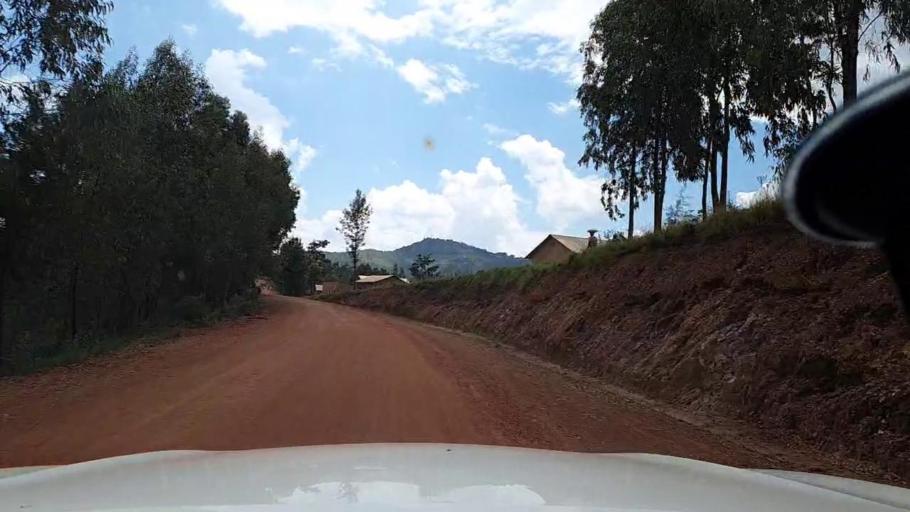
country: RW
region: Kigali
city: Kigali
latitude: -1.7618
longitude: 29.8418
